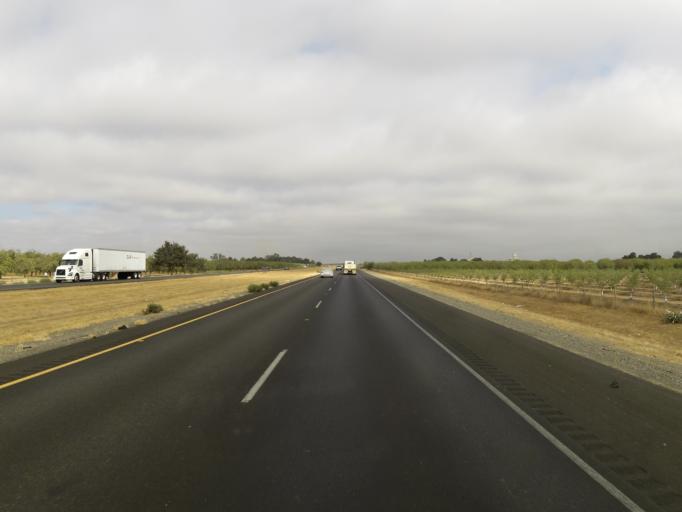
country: US
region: California
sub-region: Yolo County
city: Dunnigan
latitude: 38.9161
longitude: -121.9938
